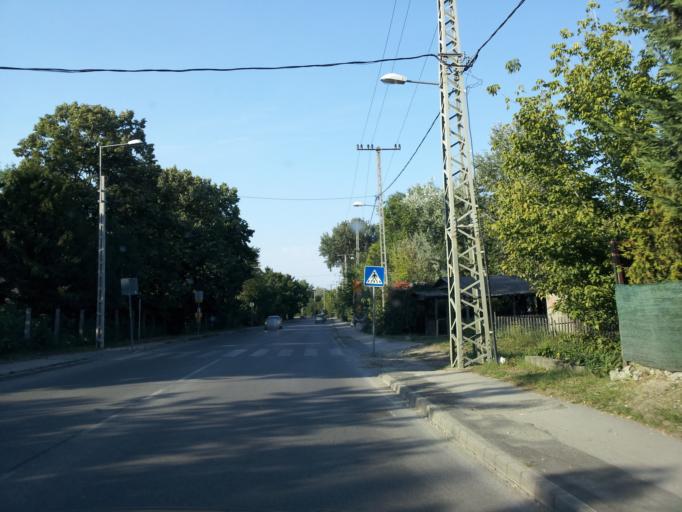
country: HU
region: Pest
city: Szentendre
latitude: 47.6904
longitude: 19.0865
